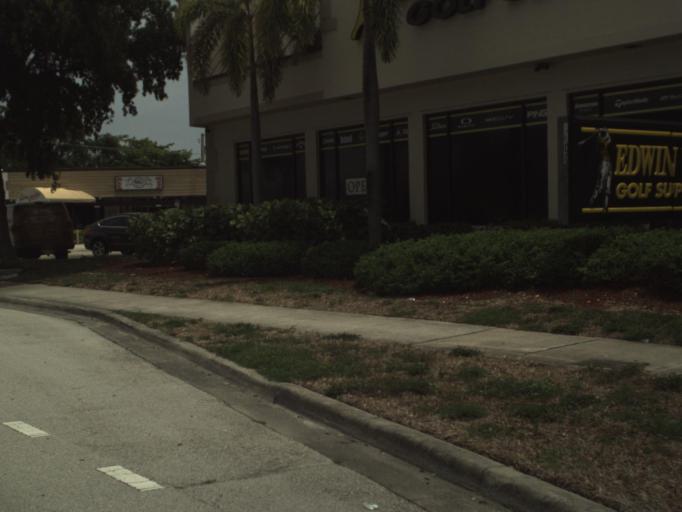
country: US
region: Florida
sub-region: Broward County
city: Lauderdale-by-the-Sea
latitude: 26.1974
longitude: -80.1110
